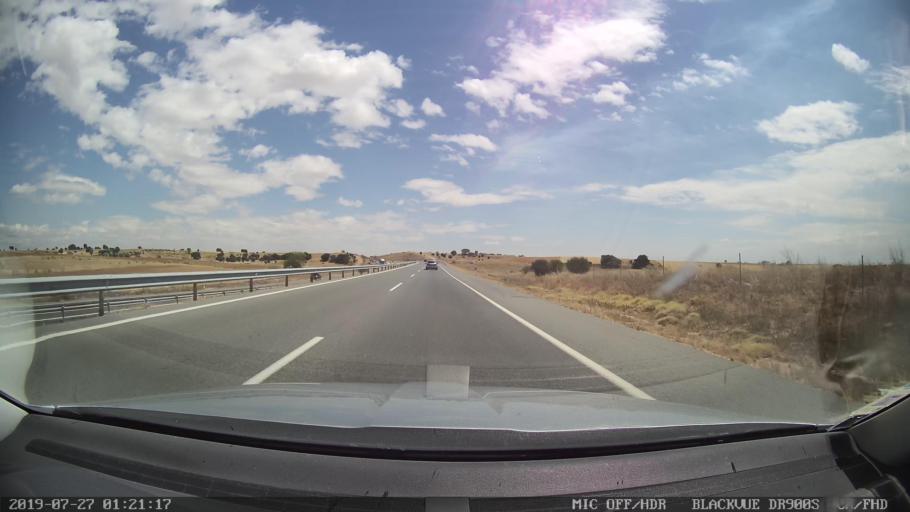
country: ES
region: Castille-La Mancha
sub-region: Province of Toledo
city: Quismondo
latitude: 40.1177
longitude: -4.2841
